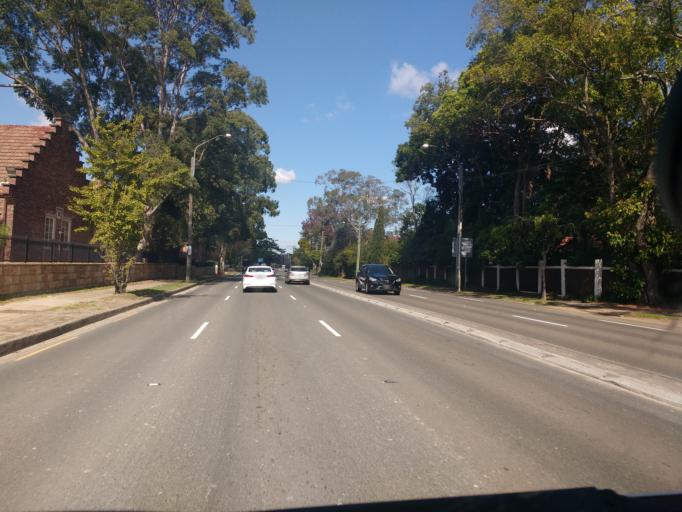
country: AU
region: New South Wales
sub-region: Ku-ring-gai
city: North Wahroonga
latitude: -33.7234
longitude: 151.1187
